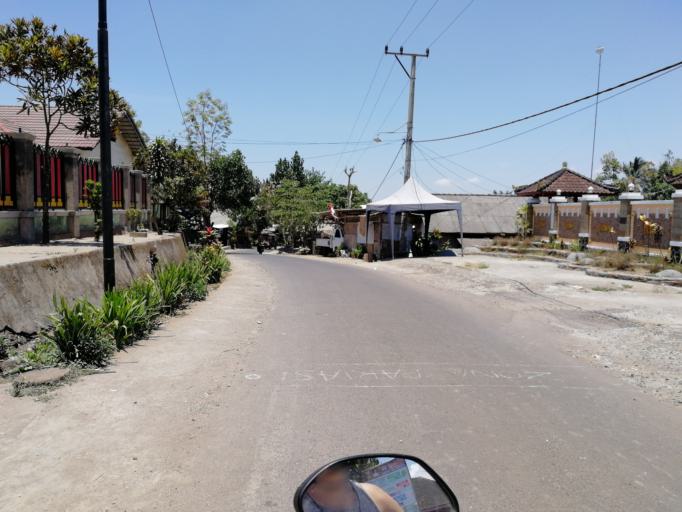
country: ID
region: West Nusa Tenggara
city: Tetebatu
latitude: -8.5534
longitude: 116.4200
